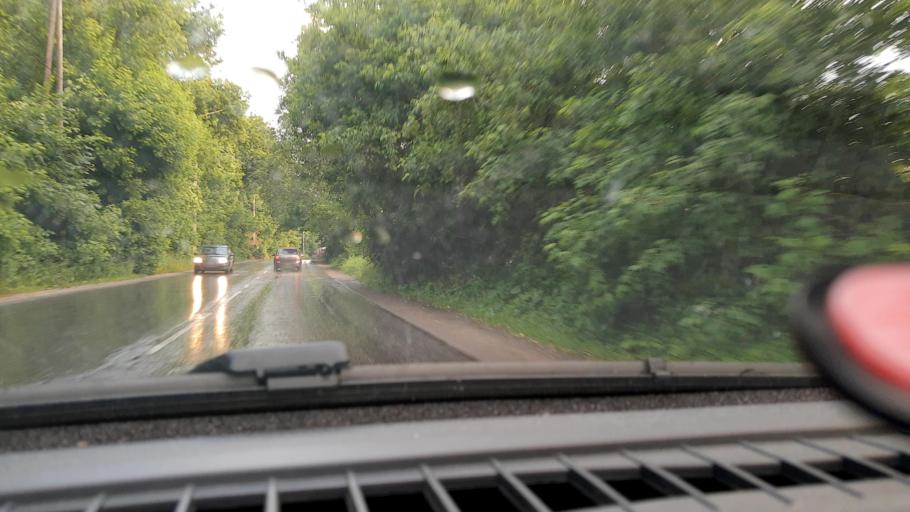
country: RU
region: Nizjnij Novgorod
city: Gorodets
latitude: 56.6498
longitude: 43.4653
